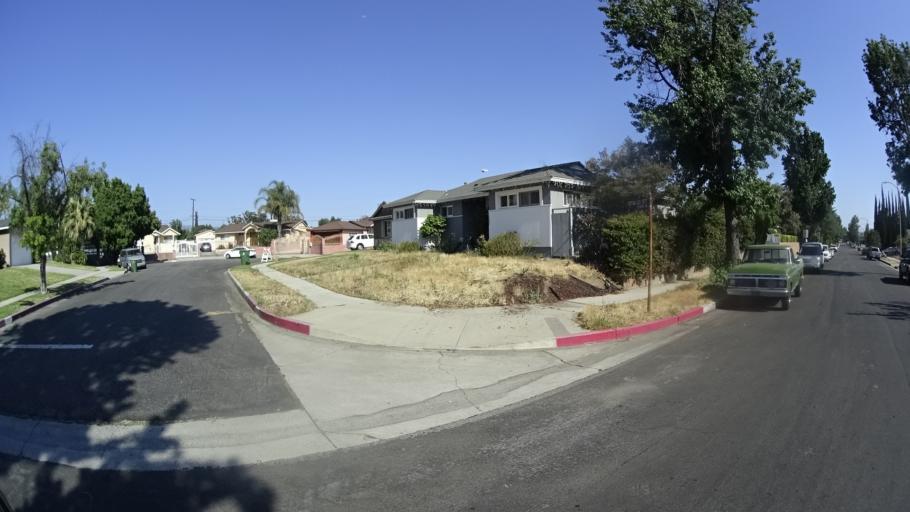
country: US
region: California
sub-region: Los Angeles County
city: Van Nuys
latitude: 34.2120
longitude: -118.4267
